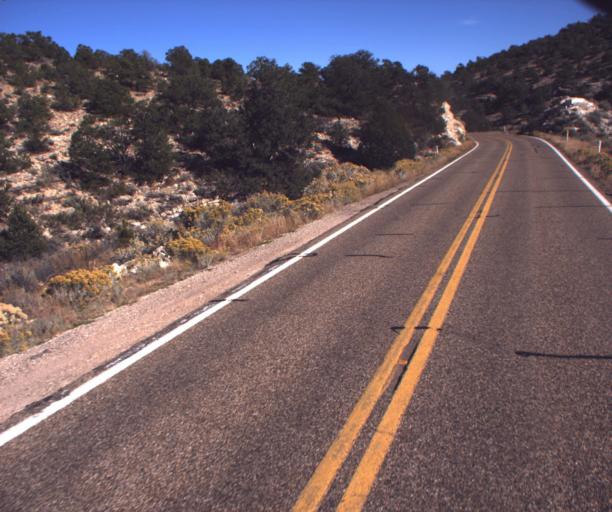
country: US
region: Arizona
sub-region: Coconino County
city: Fredonia
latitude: 36.7294
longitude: -112.0915
